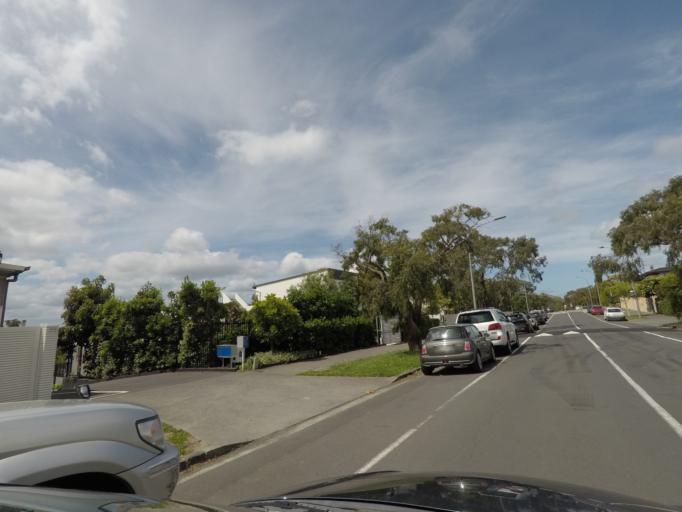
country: NZ
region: Auckland
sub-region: Auckland
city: Auckland
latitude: -36.8415
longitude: 174.7360
